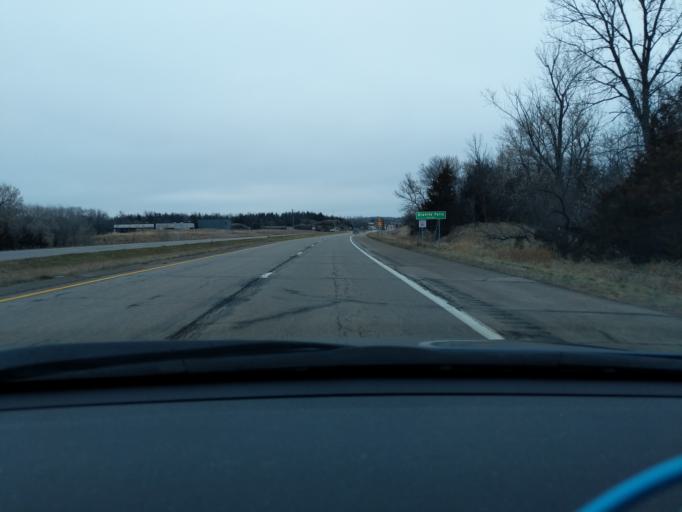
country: US
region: Minnesota
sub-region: Yellow Medicine County
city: Granite Falls
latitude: 44.7992
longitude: -95.5481
